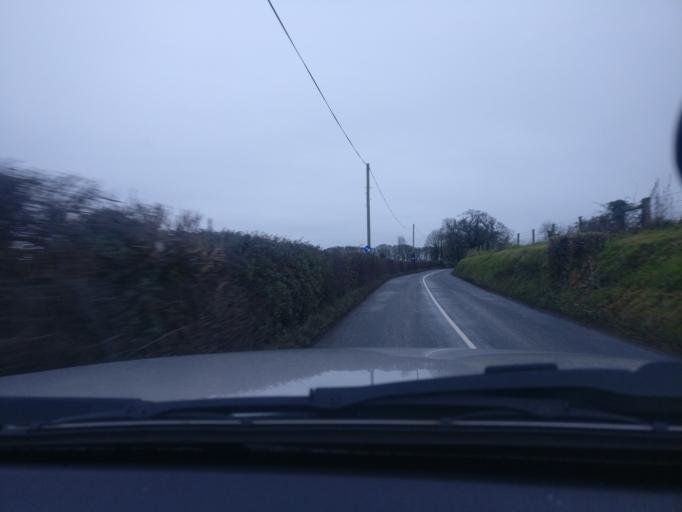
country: IE
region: Leinster
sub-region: An Mhi
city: Dunshaughlin
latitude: 53.4835
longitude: -6.6136
